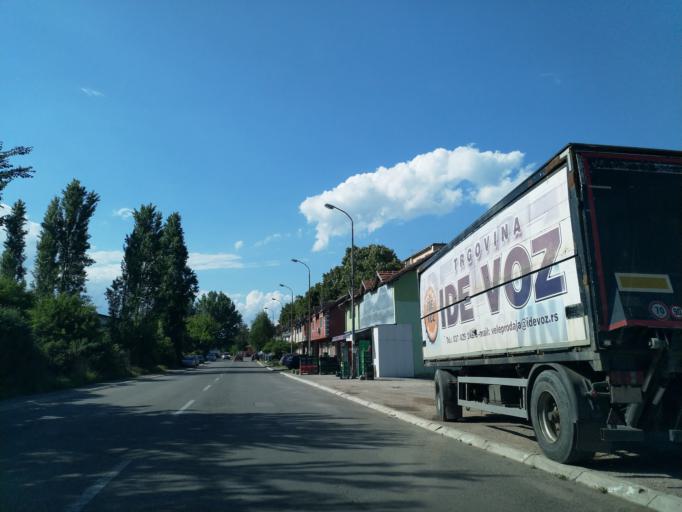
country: RS
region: Central Serbia
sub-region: Pomoravski Okrug
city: Paracin
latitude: 43.8565
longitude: 21.4067
